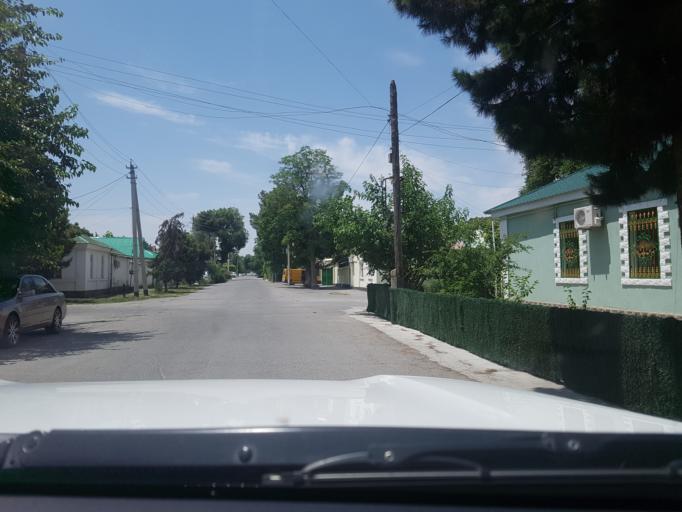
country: TM
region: Ahal
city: Ashgabat
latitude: 37.9520
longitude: 58.3622
